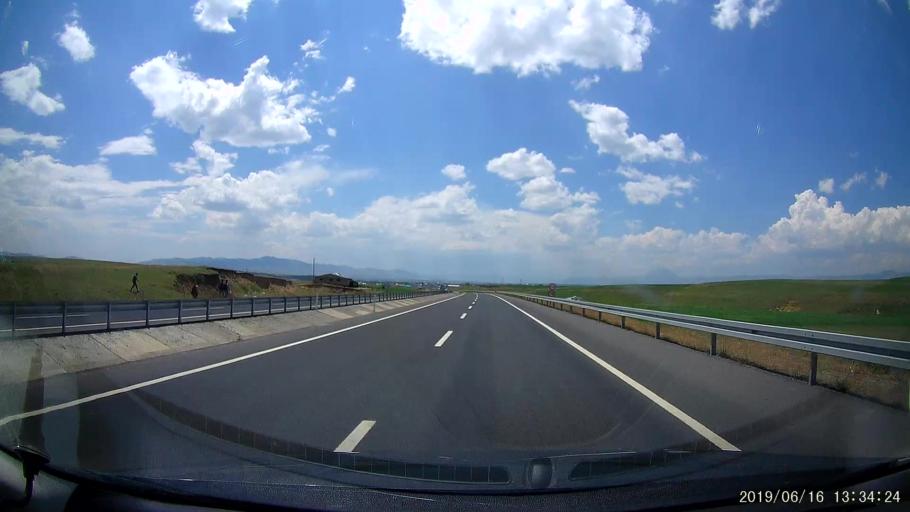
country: TR
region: Agri
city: Agri
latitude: 39.7127
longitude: 43.1276
